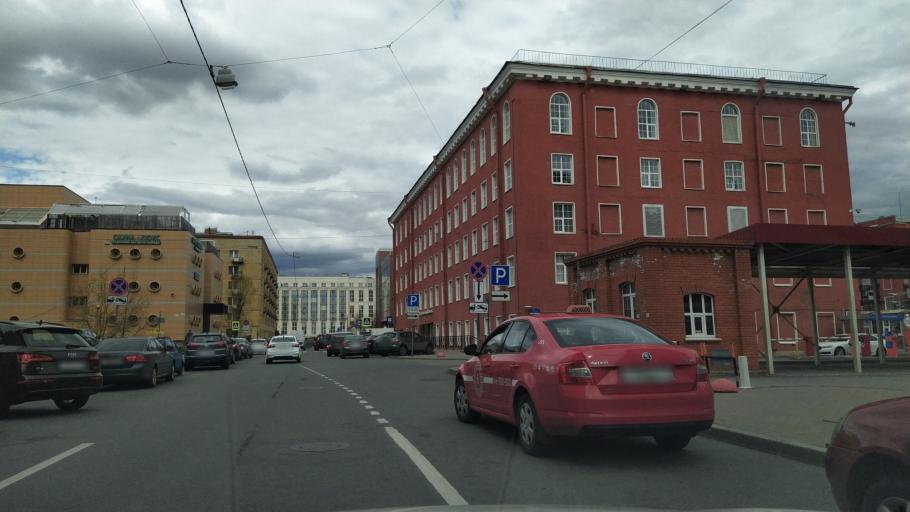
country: RU
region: St.-Petersburg
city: Centralniy
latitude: 59.9407
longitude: 30.3940
